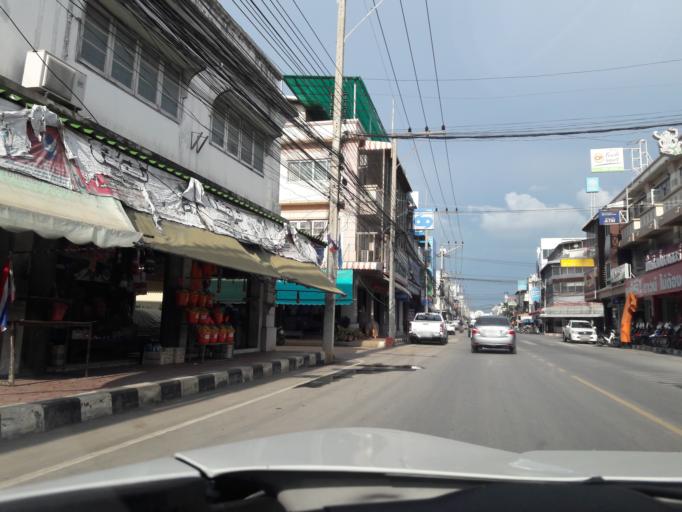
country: TH
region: Lop Buri
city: Ban Mi
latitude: 15.0416
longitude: 100.5407
